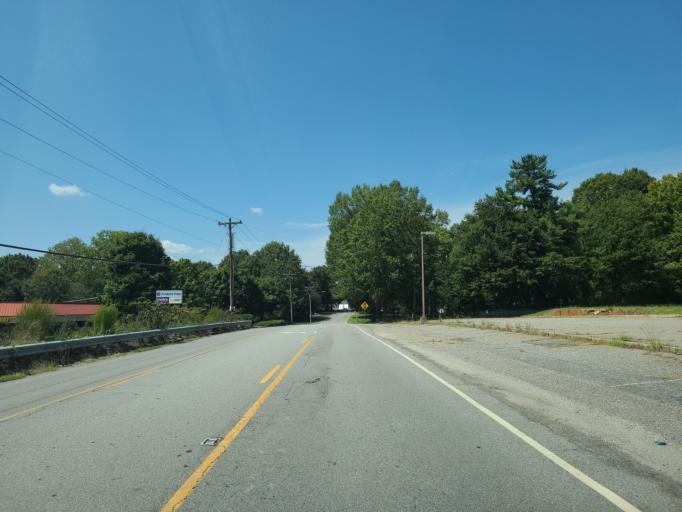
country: US
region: North Carolina
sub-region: Lincoln County
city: Lincolnton
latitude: 35.4916
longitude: -81.2466
